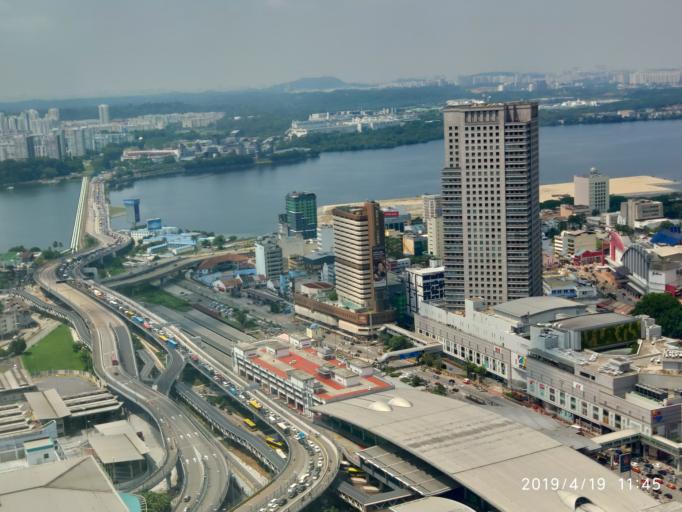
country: MY
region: Johor
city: Johor Bahru
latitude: 1.4668
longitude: 103.7647
